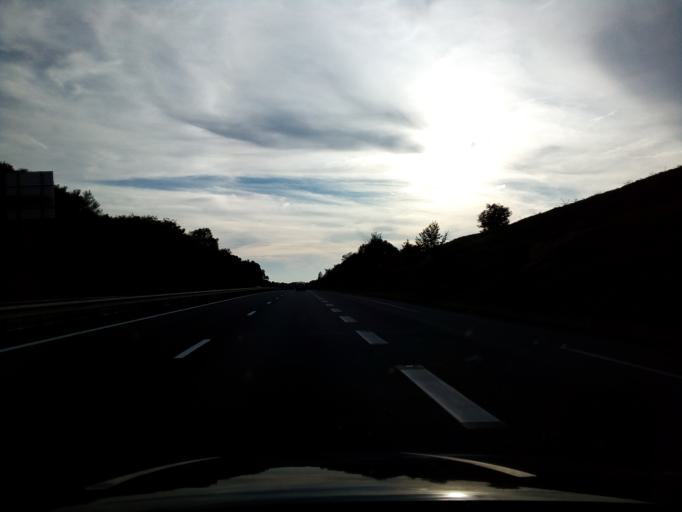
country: FR
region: Poitou-Charentes
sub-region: Departement de la Charente
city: Chasseneuil-sur-Bonnieure
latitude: 45.8103
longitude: 0.4479
